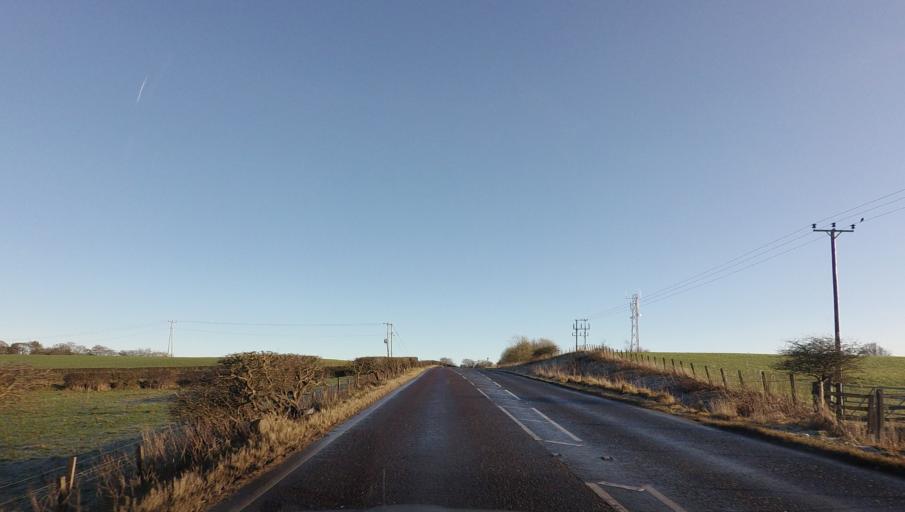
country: GB
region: Scotland
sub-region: North Lanarkshire
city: Shotts
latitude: 55.8083
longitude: -3.7964
